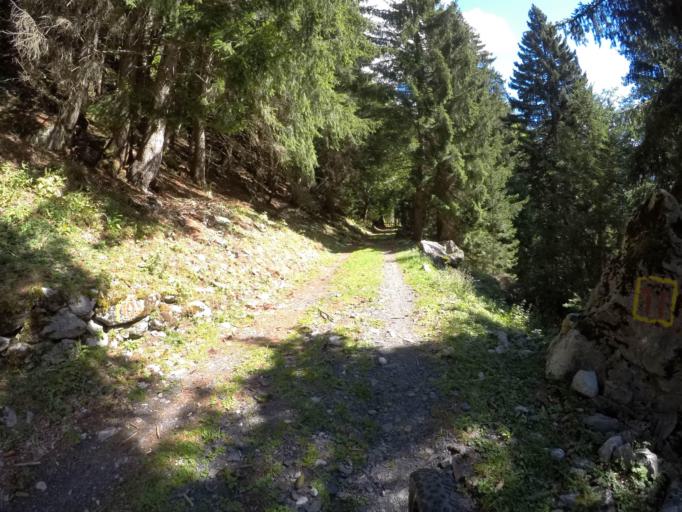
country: IT
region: Friuli Venezia Giulia
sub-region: Provincia di Udine
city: Paularo
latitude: 46.5663
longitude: 13.1238
